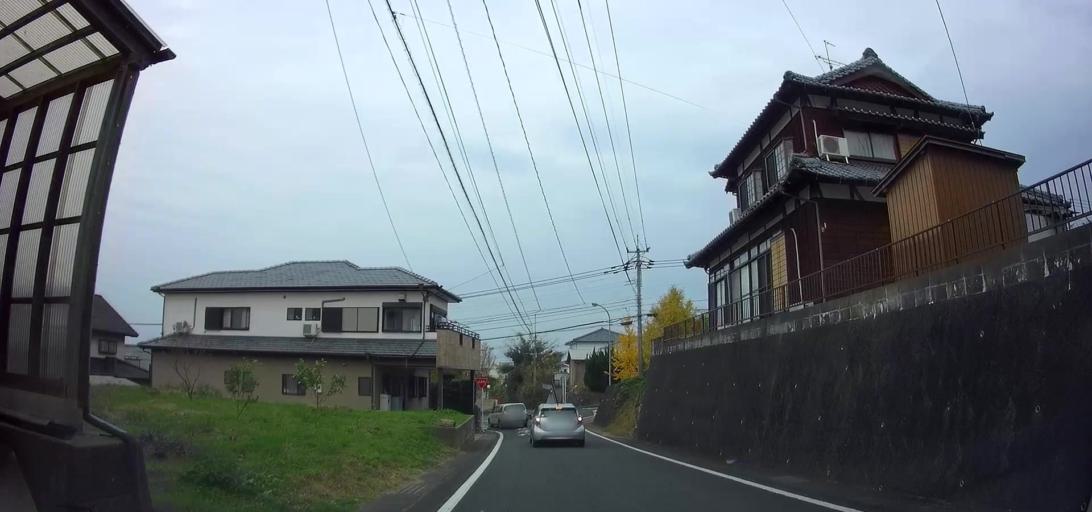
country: JP
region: Nagasaki
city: Shimabara
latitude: 32.6602
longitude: 130.2890
